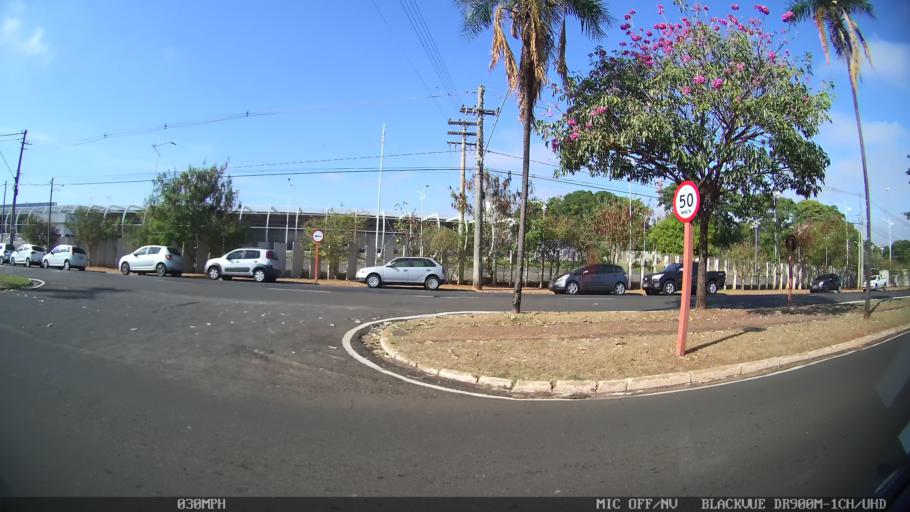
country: BR
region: Sao Paulo
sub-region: Sao Jose Do Rio Preto
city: Sao Jose do Rio Preto
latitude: -20.8125
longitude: -49.4064
